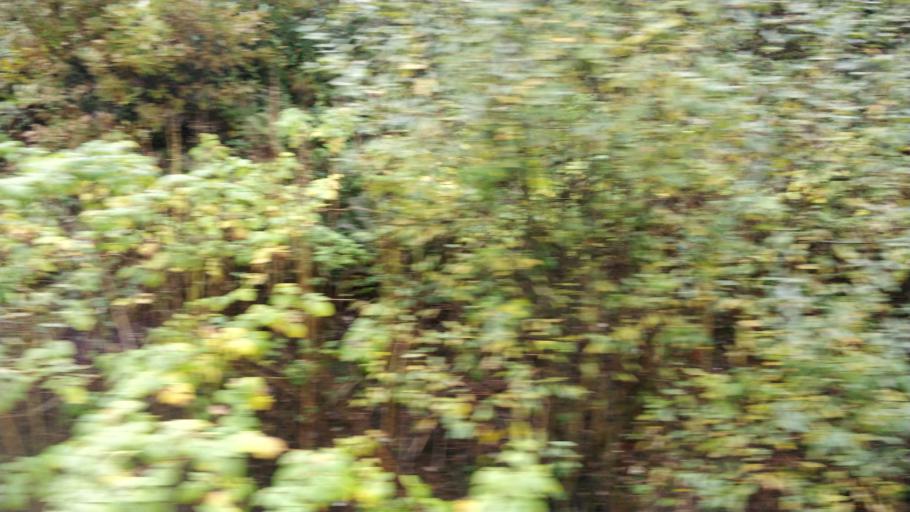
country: GB
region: England
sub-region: Borough of Wigan
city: Hindley
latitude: 53.5428
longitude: -2.5710
